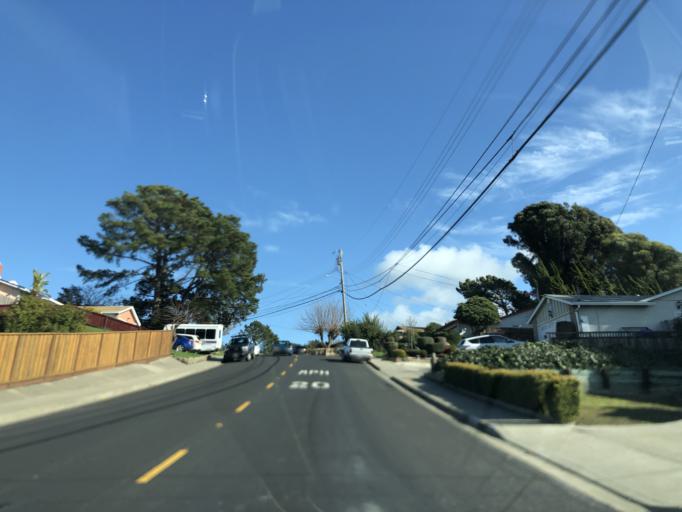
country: US
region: California
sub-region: Contra Costa County
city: Tara Hills
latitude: 37.9919
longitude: -122.3138
